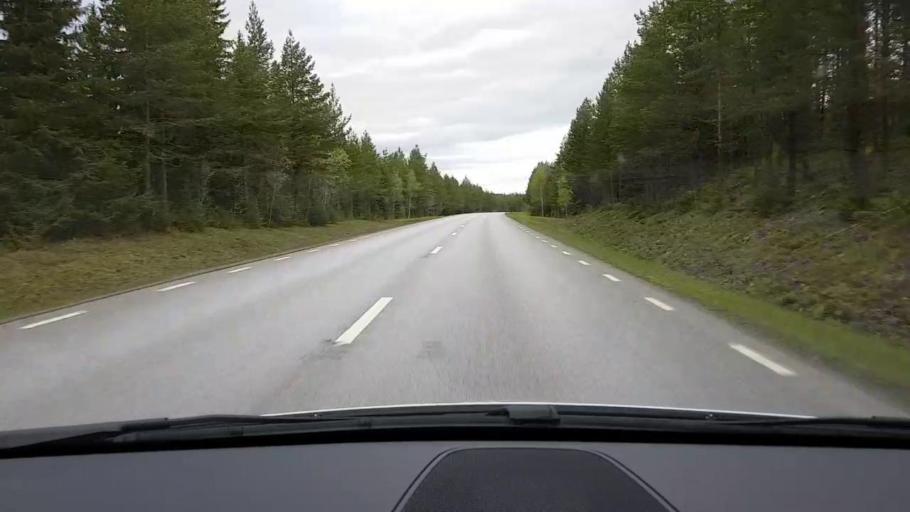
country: SE
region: Jaemtland
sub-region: Krokoms Kommun
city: Valla
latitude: 63.2797
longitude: 13.9350
